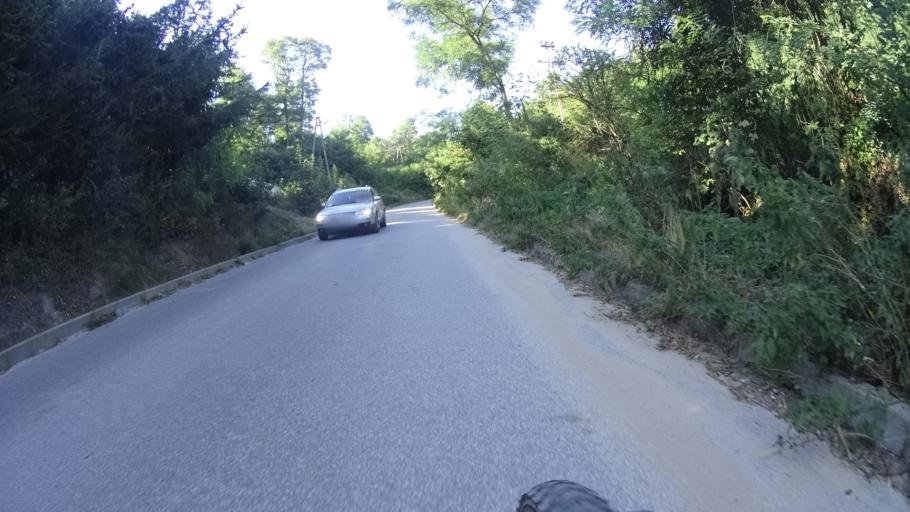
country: PL
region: Masovian Voivodeship
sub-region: Powiat bialobrzeski
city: Bialobrzegi
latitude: 51.6670
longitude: 20.8882
